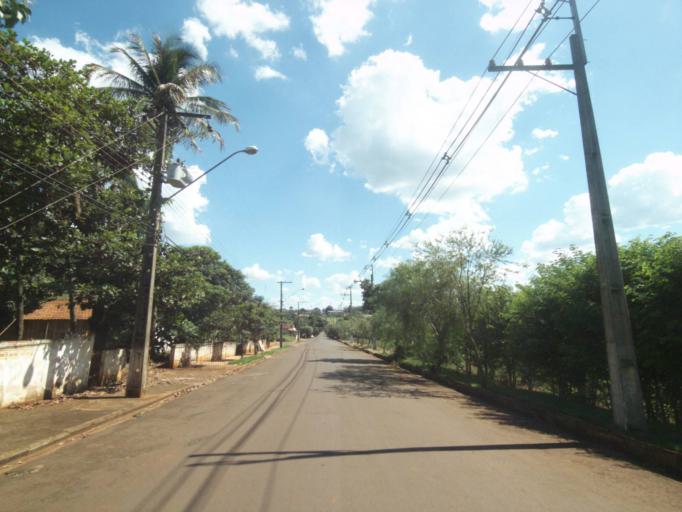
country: BR
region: Parana
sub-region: Sertanopolis
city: Sertanopolis
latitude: -23.0358
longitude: -50.8211
